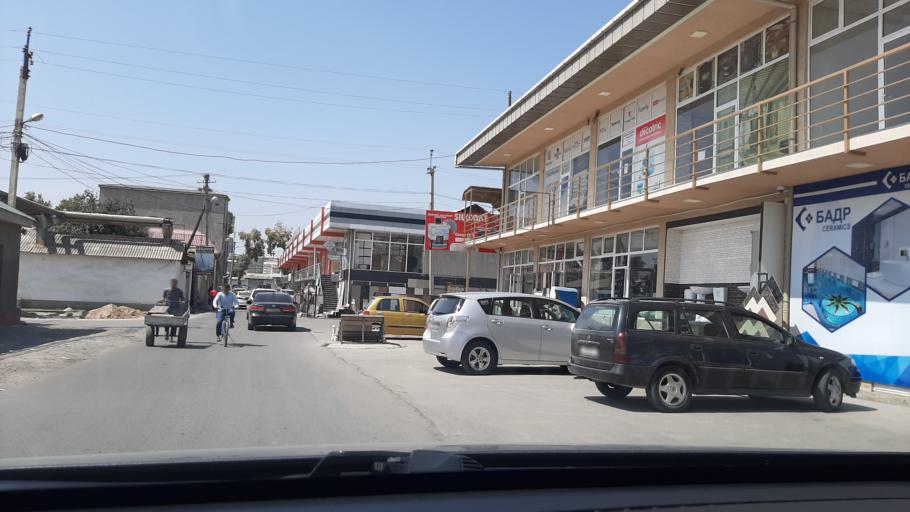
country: TJ
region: Dushanbe
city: Dushanbe
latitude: 38.5500
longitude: 68.7739
